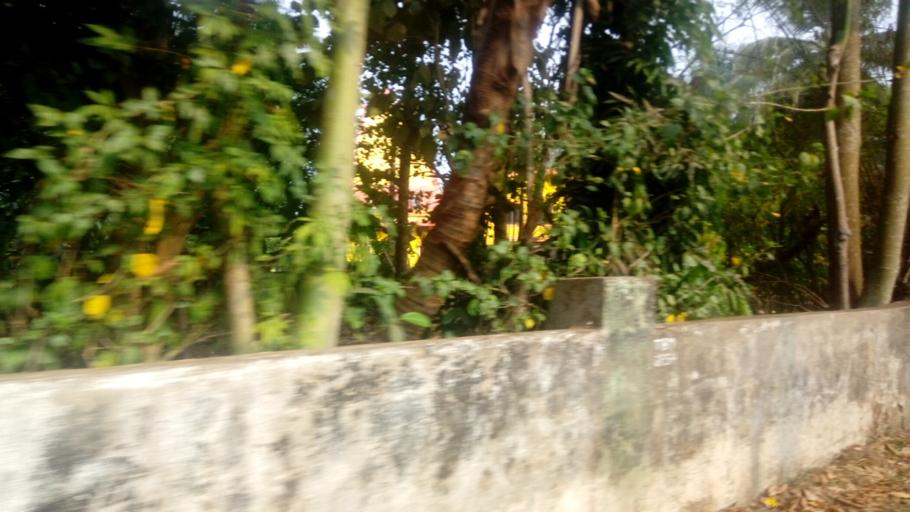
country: IN
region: Goa
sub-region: South Goa
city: Benaulim
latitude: 15.2557
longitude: 73.9329
